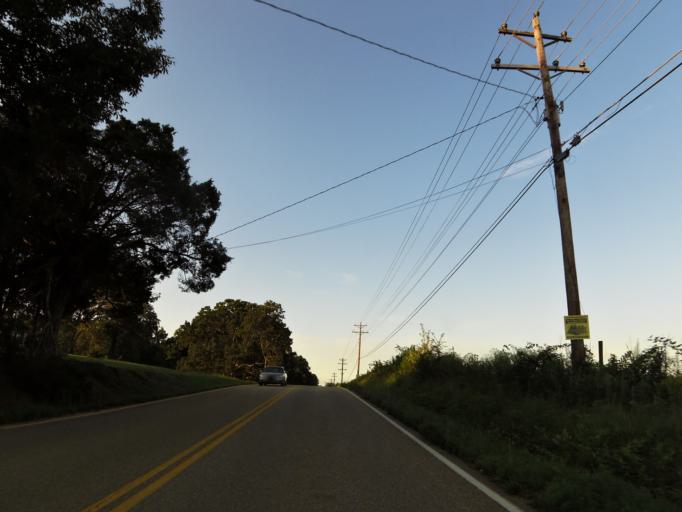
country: US
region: Tennessee
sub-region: Roane County
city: Rockwood
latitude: 35.7332
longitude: -84.6265
